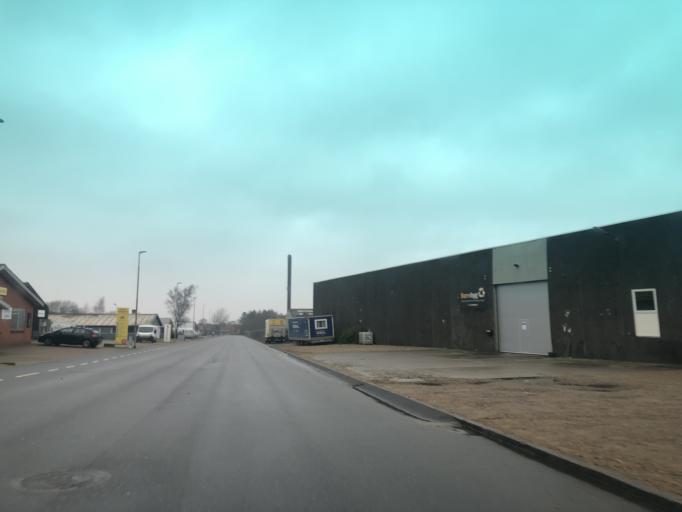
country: DK
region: Central Jutland
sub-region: Struer Kommune
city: Struer
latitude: 56.4857
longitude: 8.5786
